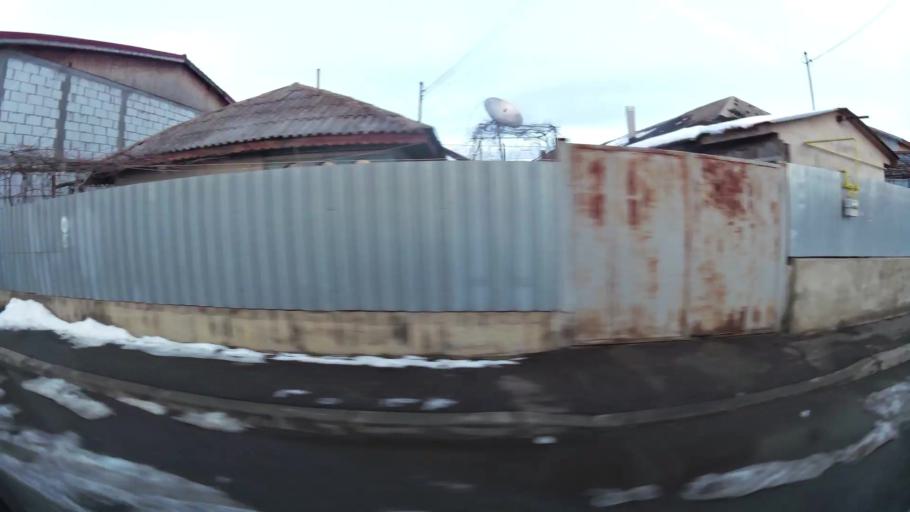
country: RO
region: Ilfov
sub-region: Comuna Magurele
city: Magurele
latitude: 44.3898
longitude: 26.0321
